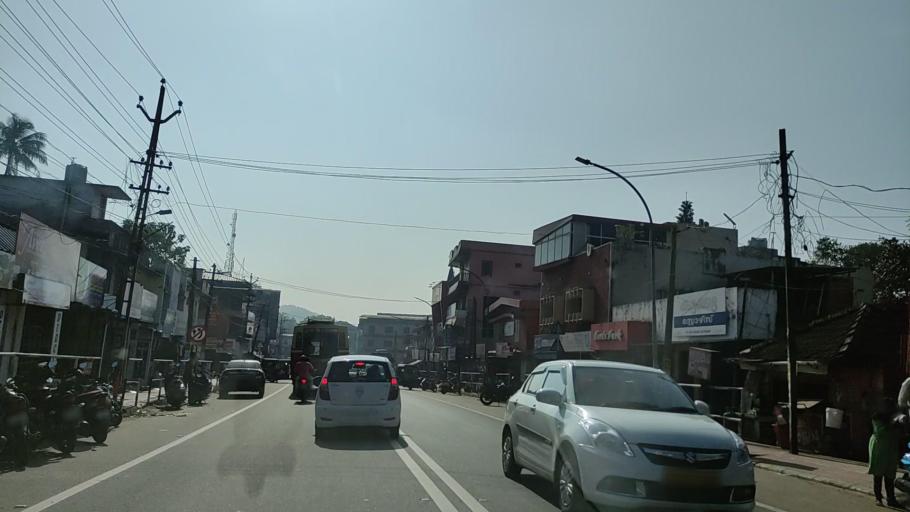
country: IN
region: Kerala
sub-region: Kollam
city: Punalur
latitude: 8.8993
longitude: 76.8590
